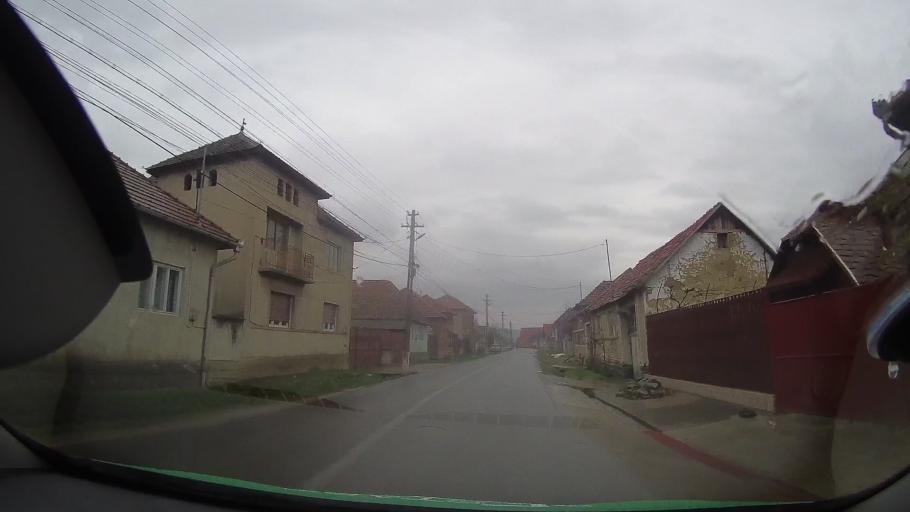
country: RO
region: Bihor
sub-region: Comuna Rabagani
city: Rabagani
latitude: 46.7466
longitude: 22.2361
